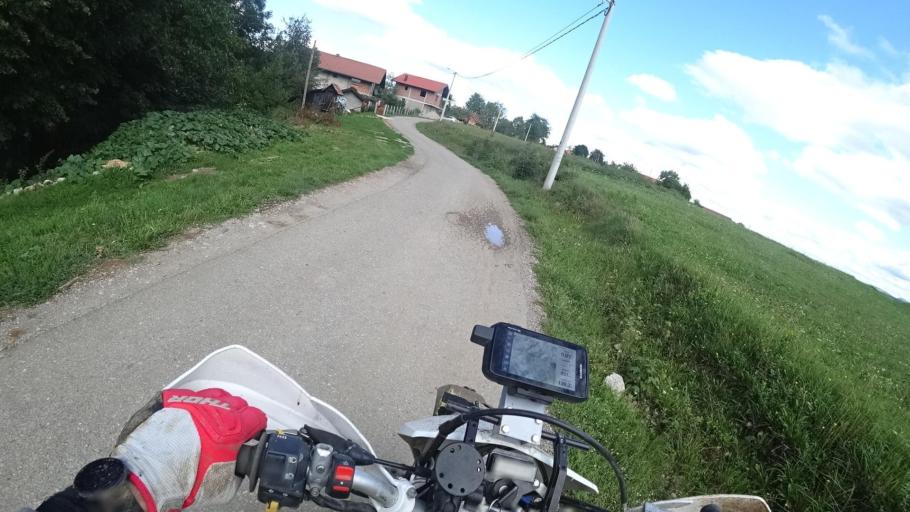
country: BA
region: Republika Srpska
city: Starcevica
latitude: 44.6692
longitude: 17.1884
